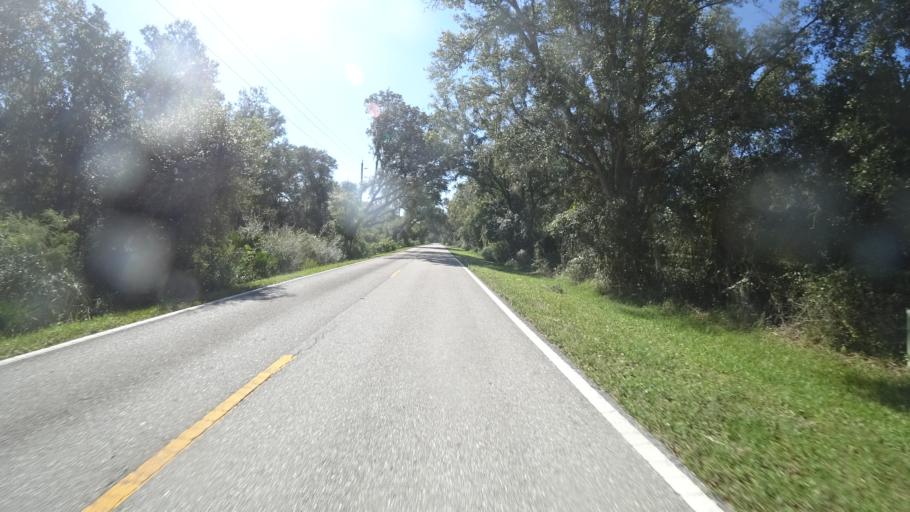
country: US
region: Florida
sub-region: Sarasota County
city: Lake Sarasota
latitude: 27.3251
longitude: -82.2694
